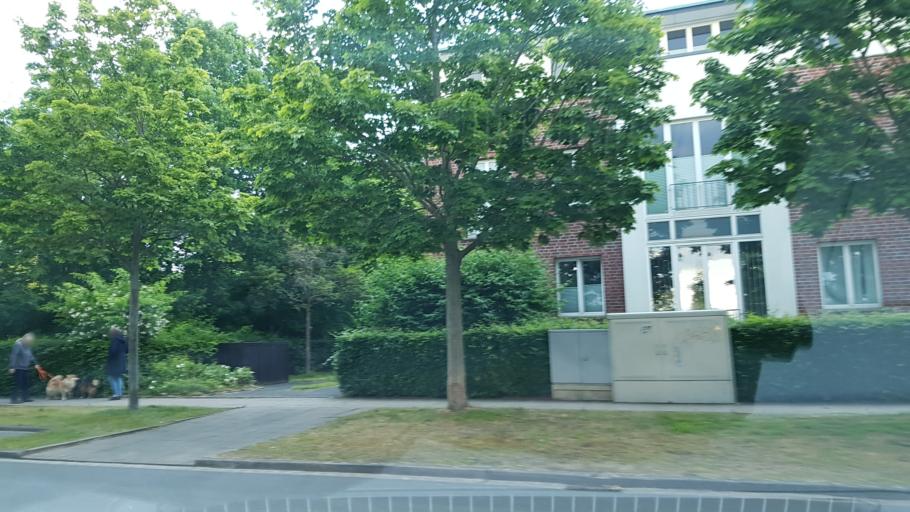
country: DE
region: Lower Saxony
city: Laatzen
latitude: 52.3474
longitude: 9.8107
